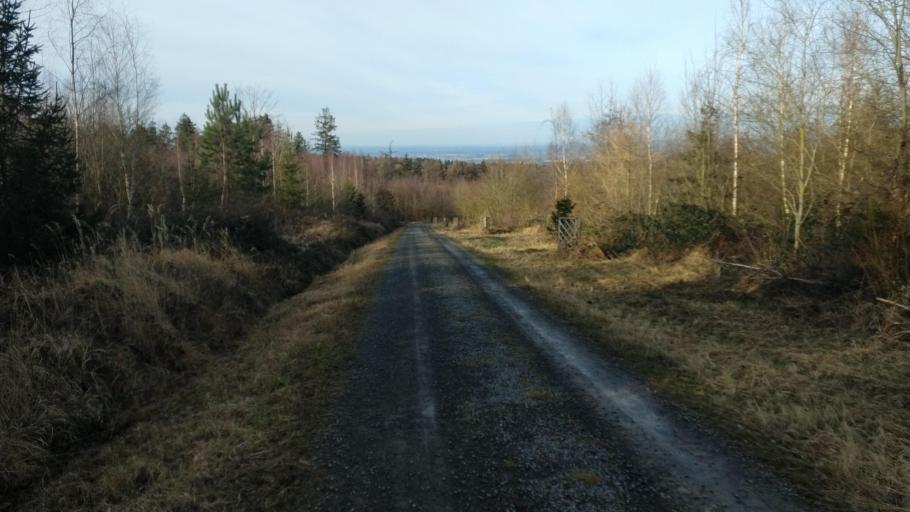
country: DE
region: Lower Saxony
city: Nienstadt
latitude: 52.2698
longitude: 9.1931
